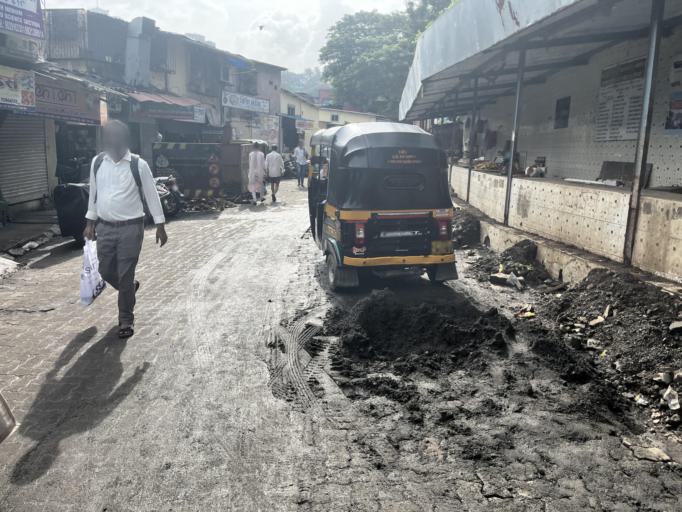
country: IN
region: Maharashtra
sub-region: Mumbai Suburban
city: Borivli
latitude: 19.2349
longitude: 72.8677
